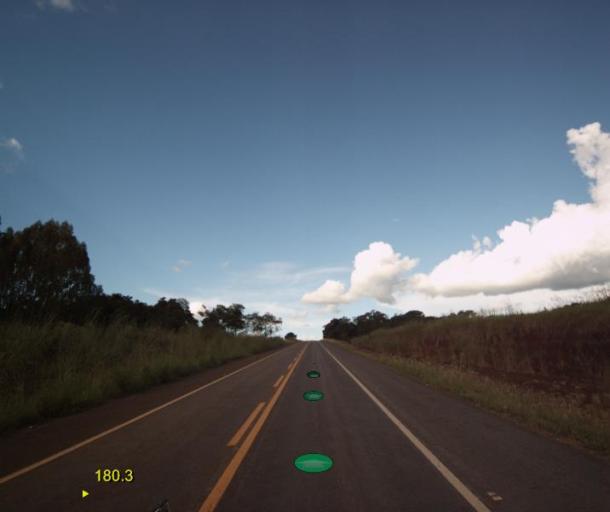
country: BR
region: Goias
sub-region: Itaberai
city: Itaberai
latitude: -15.9864
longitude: -49.7095
